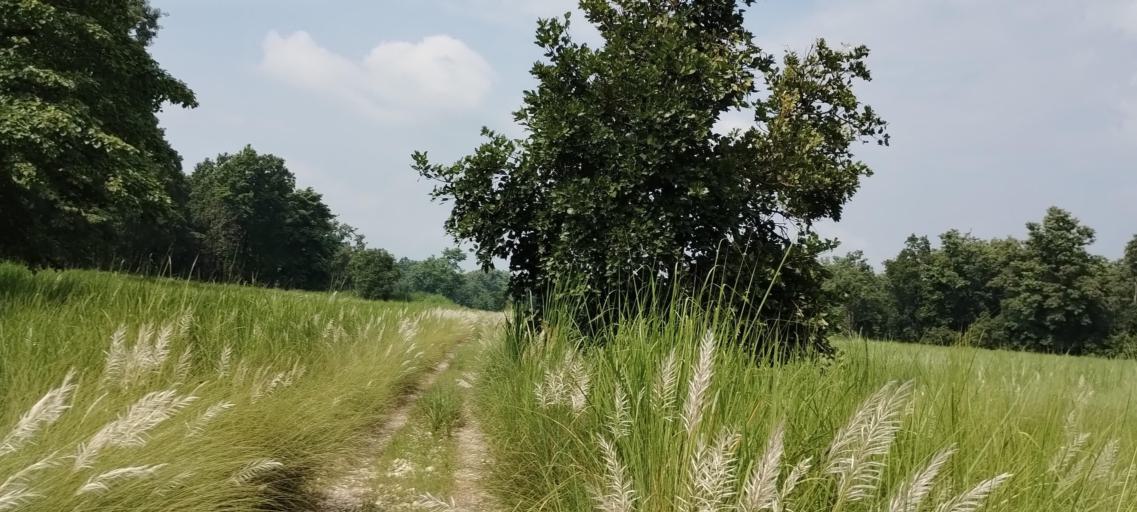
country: NP
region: Far Western
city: Tikapur
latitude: 28.5095
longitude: 81.2518
